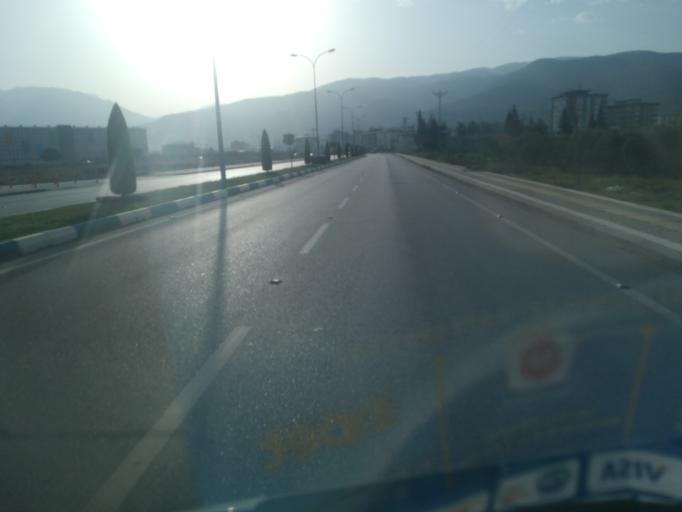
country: TR
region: Osmaniye
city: Osmaniye
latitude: 37.0515
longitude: 36.2258
